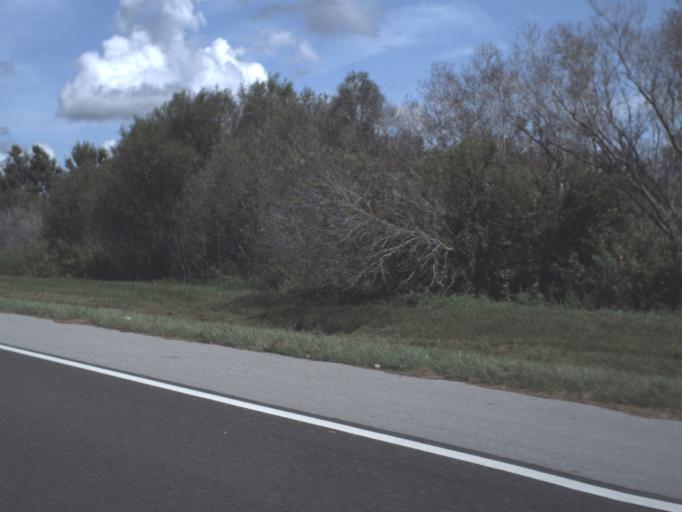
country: US
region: Florida
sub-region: Sarasota County
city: Nokomis
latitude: 27.1423
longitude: -82.4110
